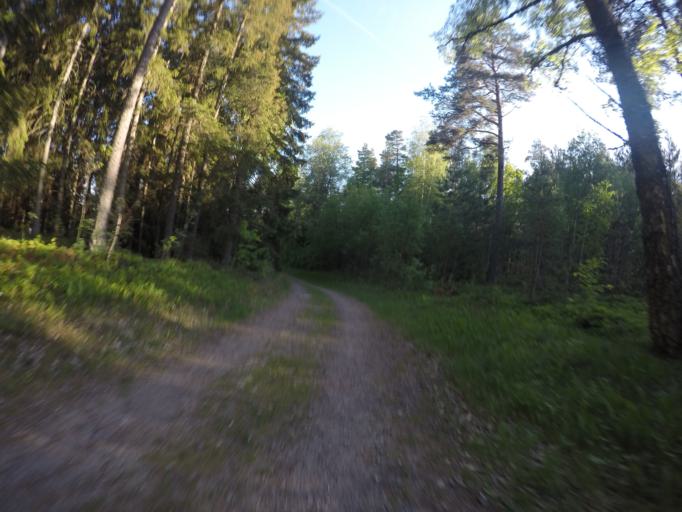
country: SE
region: Soedermanland
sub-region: Eskilstuna Kommun
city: Eskilstuna
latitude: 59.3419
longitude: 16.5277
